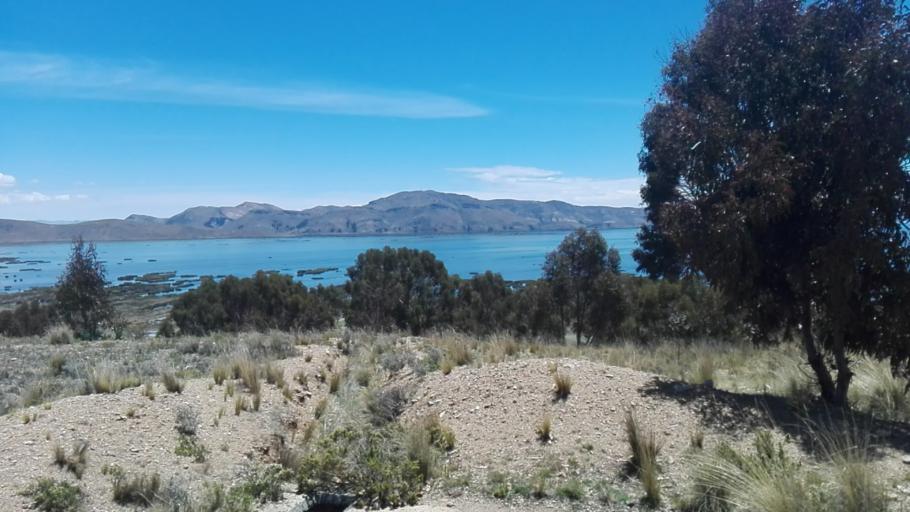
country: BO
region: La Paz
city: Batallas
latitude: -16.2931
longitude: -68.5991
